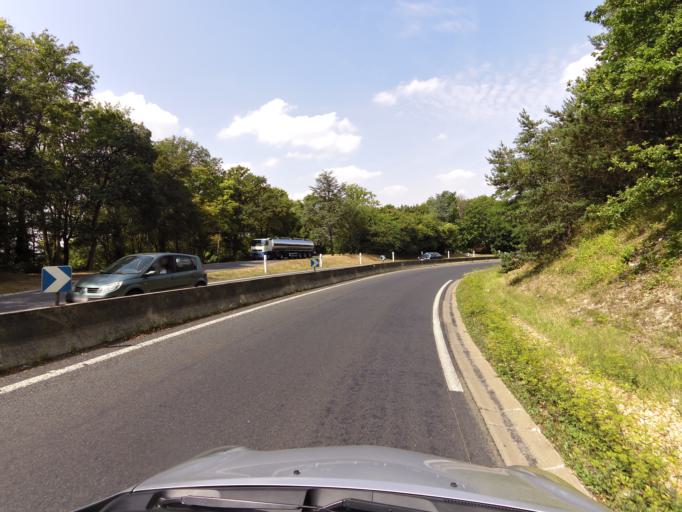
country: FR
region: Champagne-Ardenne
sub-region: Departement de la Marne
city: Rilly-la-Montagne
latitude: 49.1597
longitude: 4.0085
